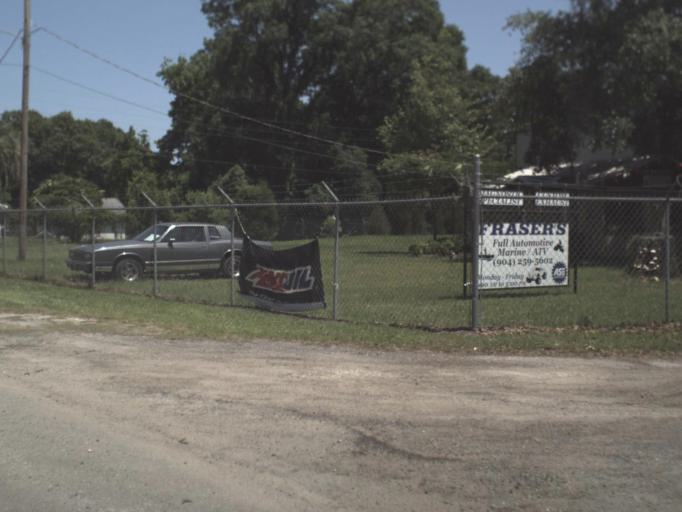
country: US
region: Florida
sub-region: Baker County
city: Macclenny
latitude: 30.2757
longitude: -82.1658
